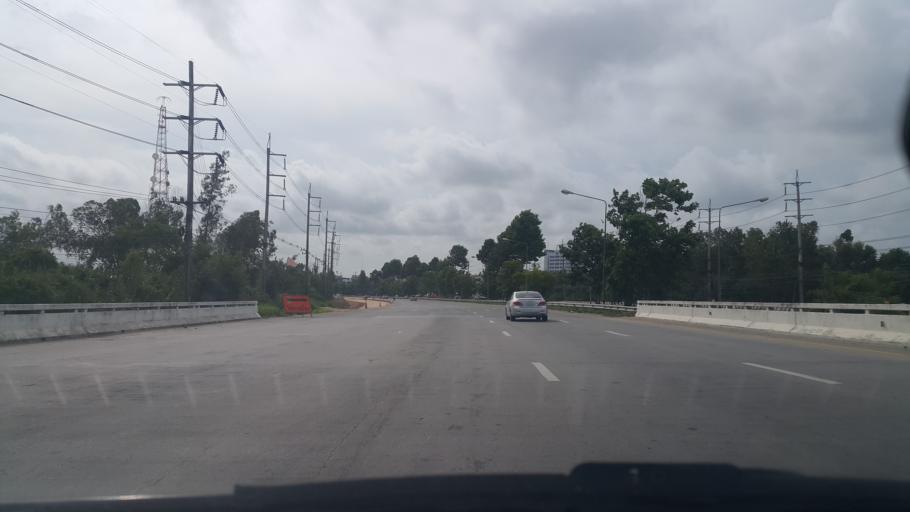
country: TH
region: Rayong
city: Rayong
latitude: 12.6896
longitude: 101.2962
